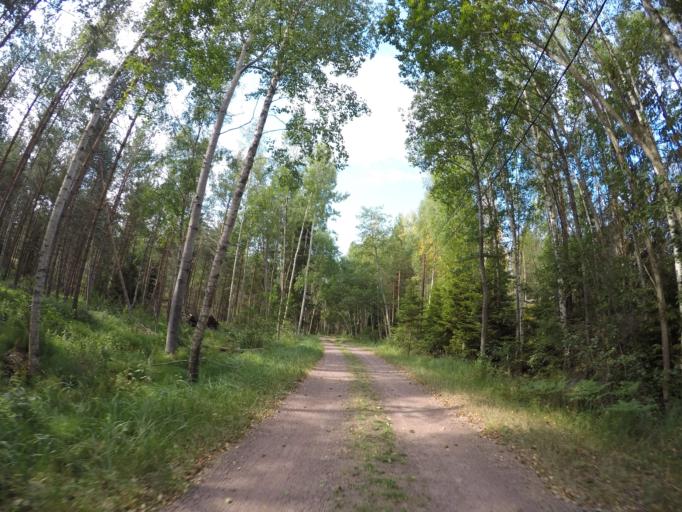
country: AX
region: Alands landsbygd
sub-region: Hammarland
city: Hammarland
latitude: 60.2240
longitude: 19.8313
